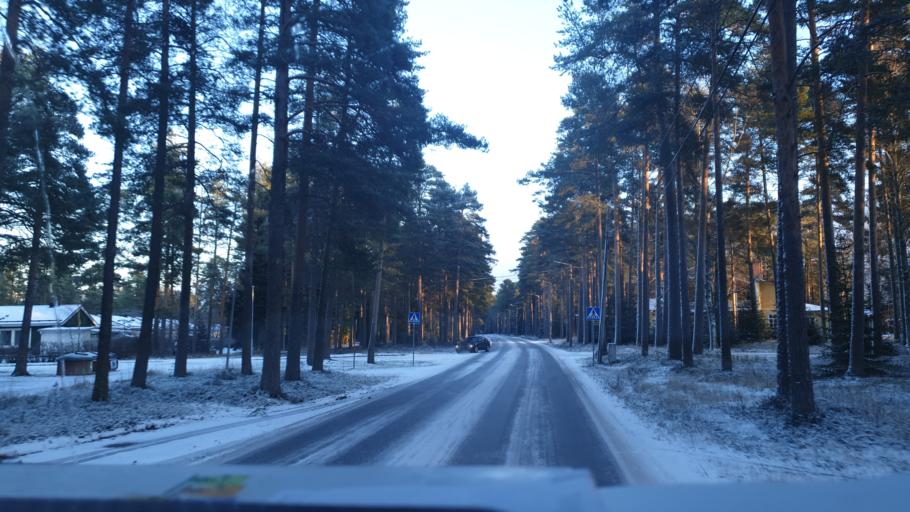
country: FI
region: Central Ostrobothnia
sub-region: Kokkola
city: Kokkola
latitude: 63.8202
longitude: 23.0785
